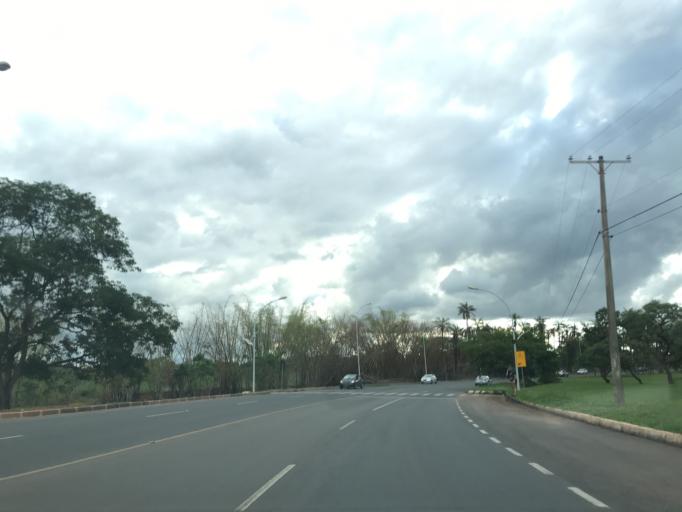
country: BR
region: Federal District
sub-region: Brasilia
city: Brasilia
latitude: -15.8139
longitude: -47.9232
